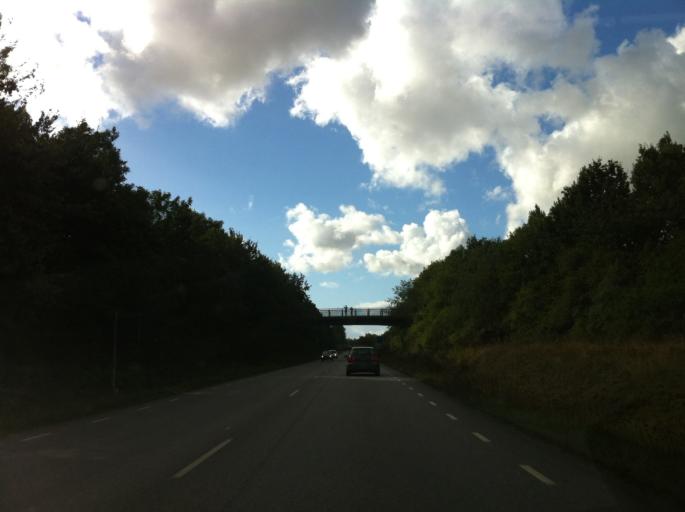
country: SE
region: Skane
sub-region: Kavlinge Kommun
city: Kaevlinge
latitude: 55.7979
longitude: 13.1396
